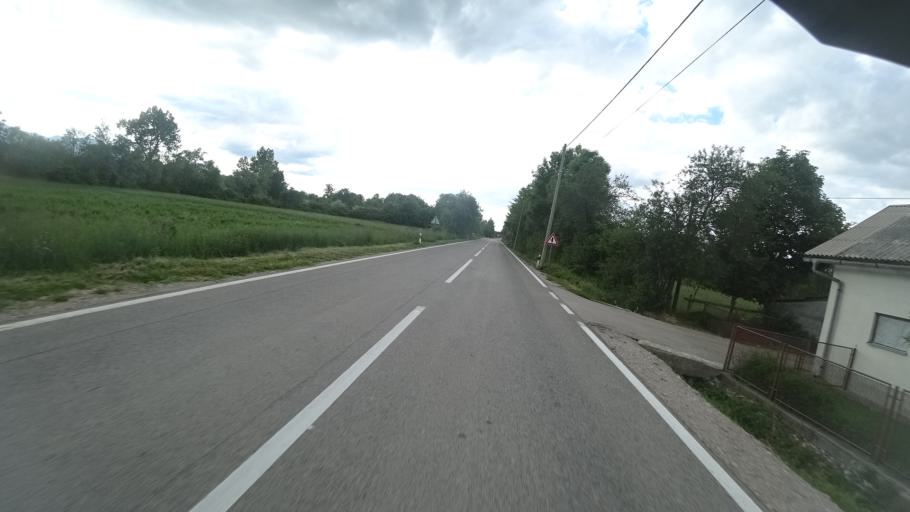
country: HR
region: Licko-Senjska
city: Gospic
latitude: 44.4865
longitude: 15.4660
